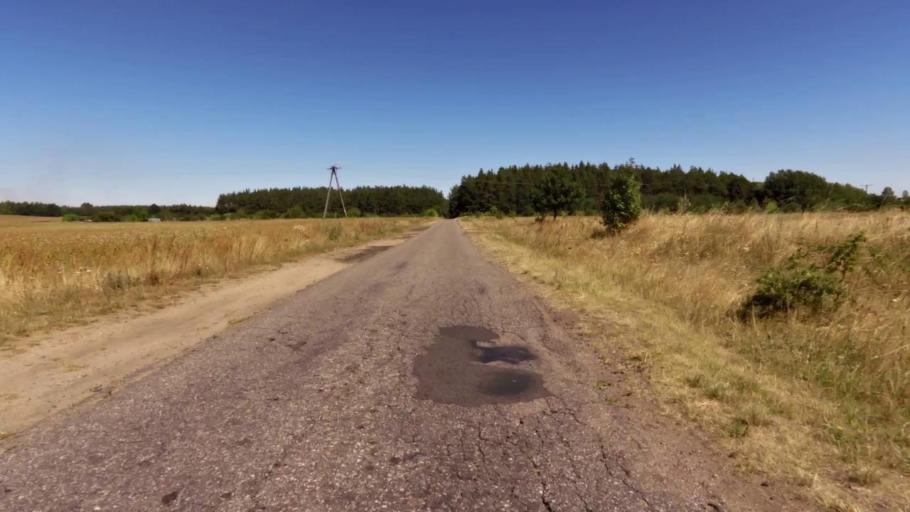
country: PL
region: West Pomeranian Voivodeship
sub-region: Powiat szczecinecki
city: Szczecinek
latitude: 53.6425
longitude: 16.7139
